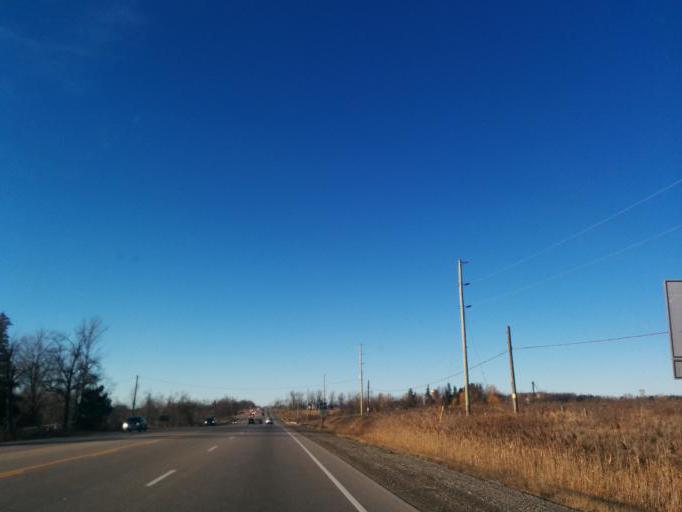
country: CA
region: Ontario
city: Brampton
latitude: 43.7485
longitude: -79.8443
